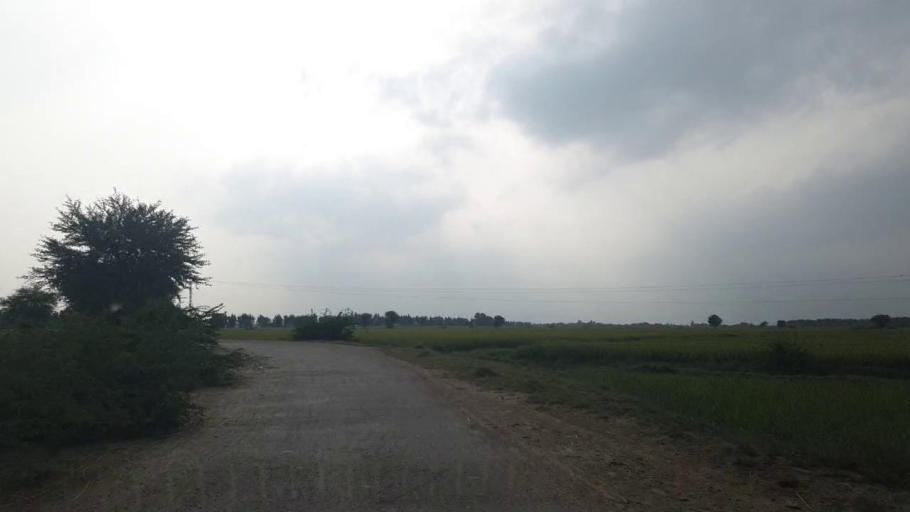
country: PK
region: Sindh
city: Badin
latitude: 24.6422
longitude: 68.6944
